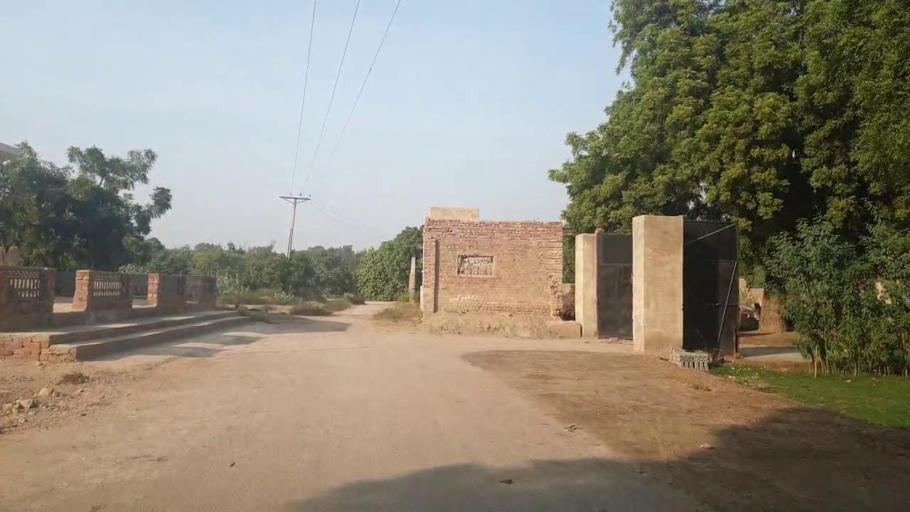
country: PK
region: Sindh
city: Tando Jam
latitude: 25.4303
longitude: 68.4648
